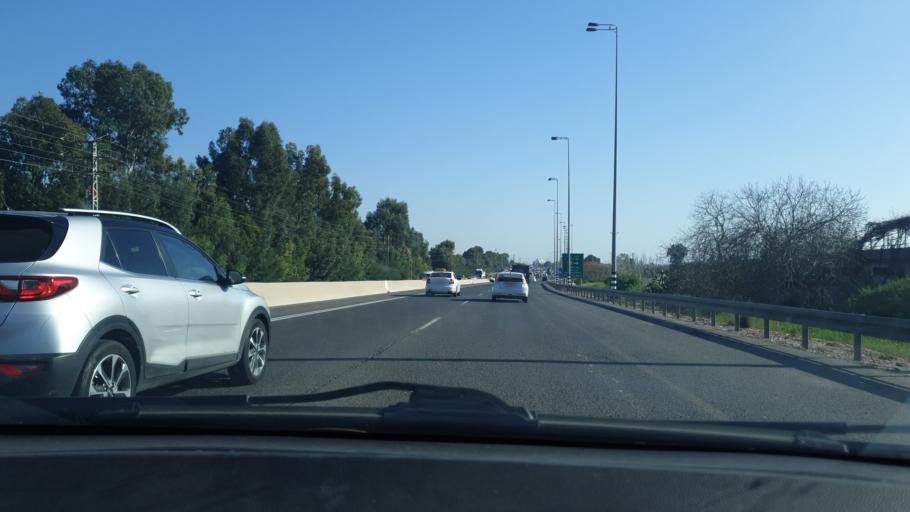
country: IL
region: Central District
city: Ramla
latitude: 31.9563
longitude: 34.8540
